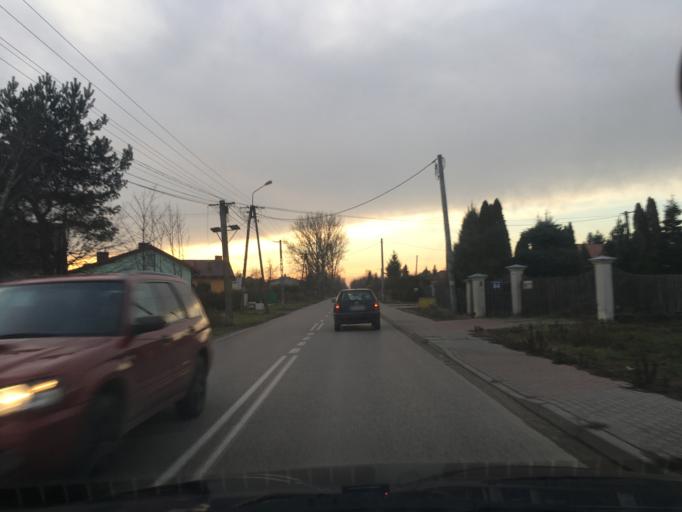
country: PL
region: Masovian Voivodeship
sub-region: Powiat piaseczynski
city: Lesznowola
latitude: 52.0419
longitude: 20.9675
